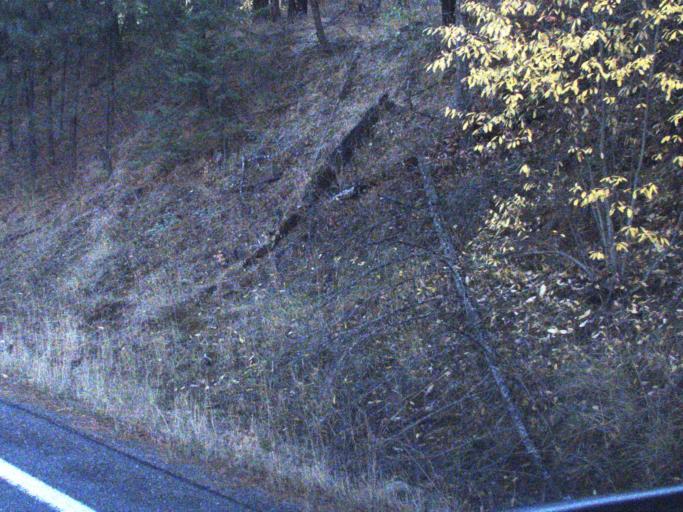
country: US
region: Washington
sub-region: Stevens County
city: Kettle Falls
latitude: 48.6606
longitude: -118.0781
